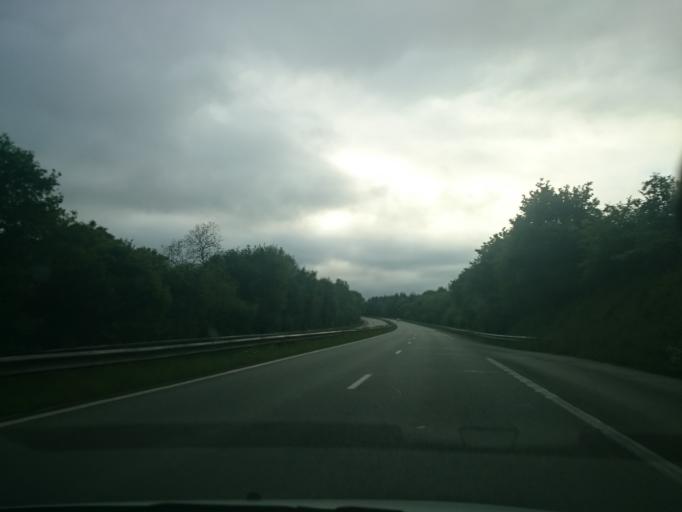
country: FR
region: Brittany
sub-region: Departement du Finistere
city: Saint-Yvi
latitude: 47.9364
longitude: -3.9114
